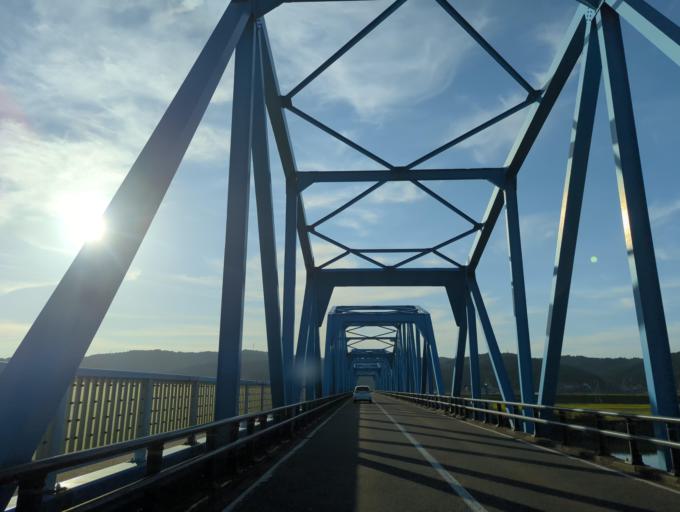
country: JP
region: Niigata
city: Nagaoka
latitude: 37.5532
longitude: 138.8214
